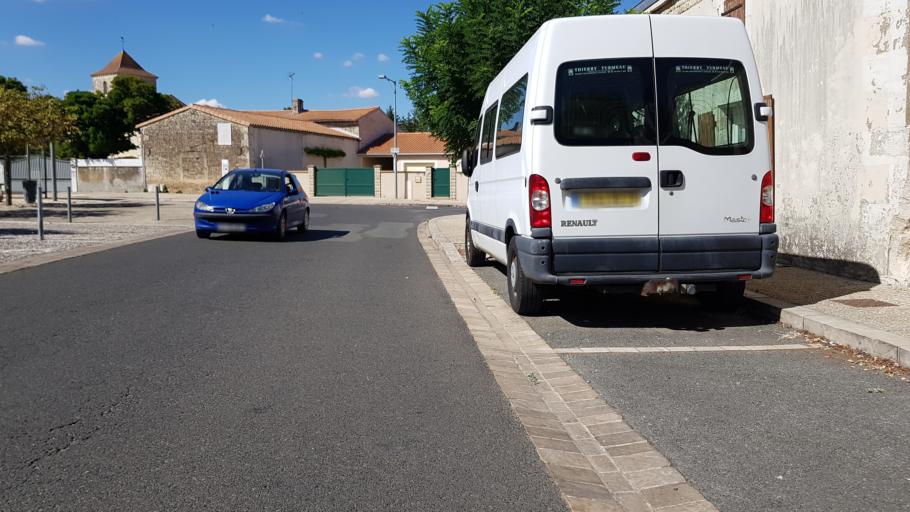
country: FR
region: Poitou-Charentes
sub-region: Departement des Deux-Sevres
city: Vouille
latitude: 46.3142
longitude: -0.3666
